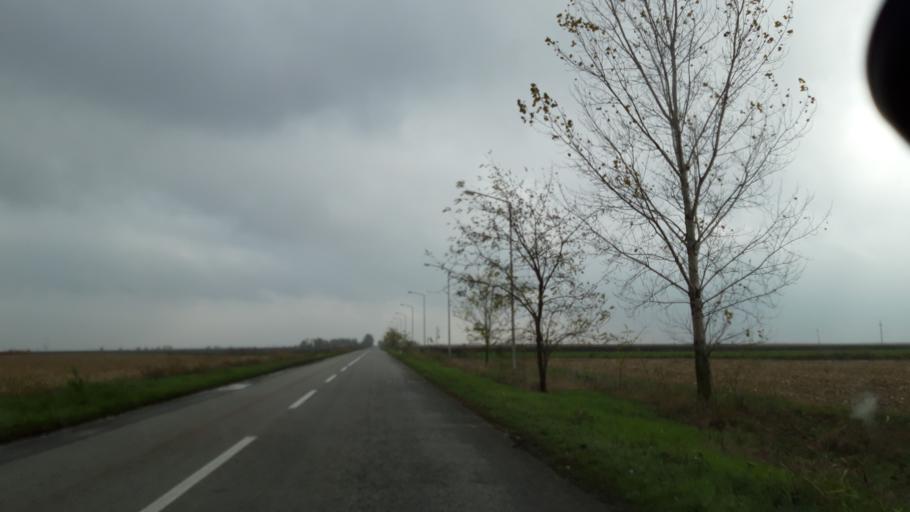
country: RS
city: Backo Gradiste
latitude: 45.5035
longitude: 19.9382
